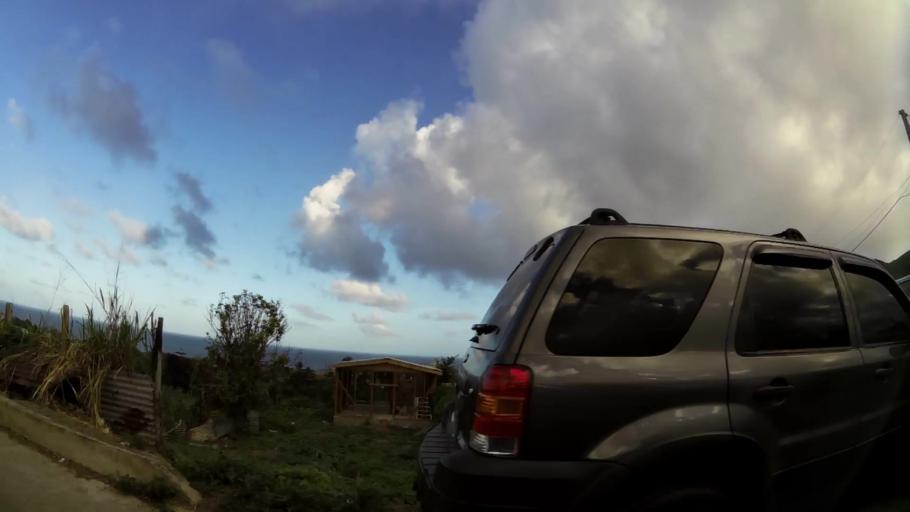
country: KN
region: Saint Mary Cayon
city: Cayon
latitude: 17.3513
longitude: -62.7302
